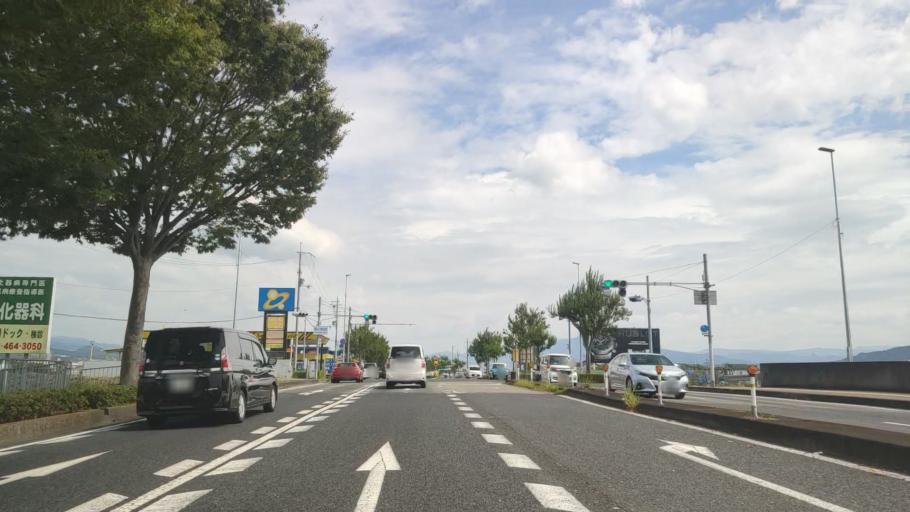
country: JP
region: Wakayama
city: Iwade
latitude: 34.2639
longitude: 135.2760
